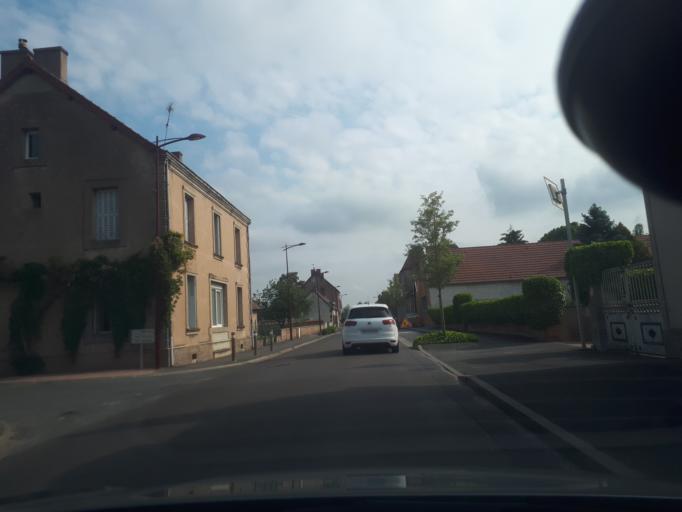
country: FR
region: Auvergne
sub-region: Departement de l'Allier
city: Dompierre-sur-Besbre
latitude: 46.4473
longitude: 3.6309
